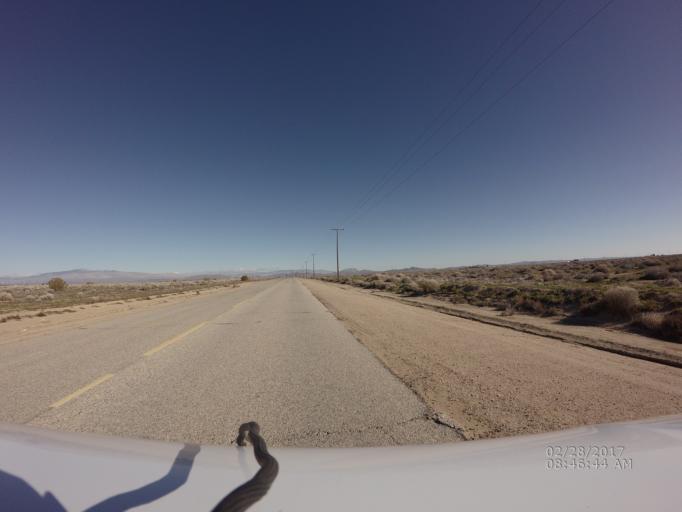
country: US
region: California
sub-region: Kern County
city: Rosamond
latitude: 34.7722
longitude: -118.2373
